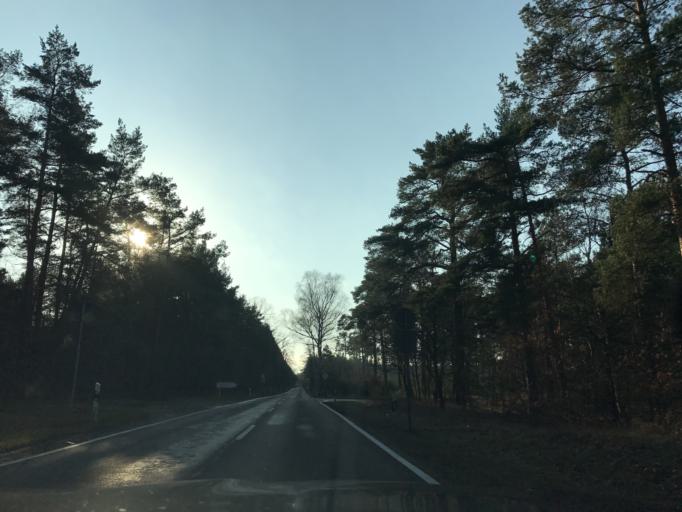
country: DE
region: Brandenburg
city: Wenzlow
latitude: 52.3333
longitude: 12.4933
